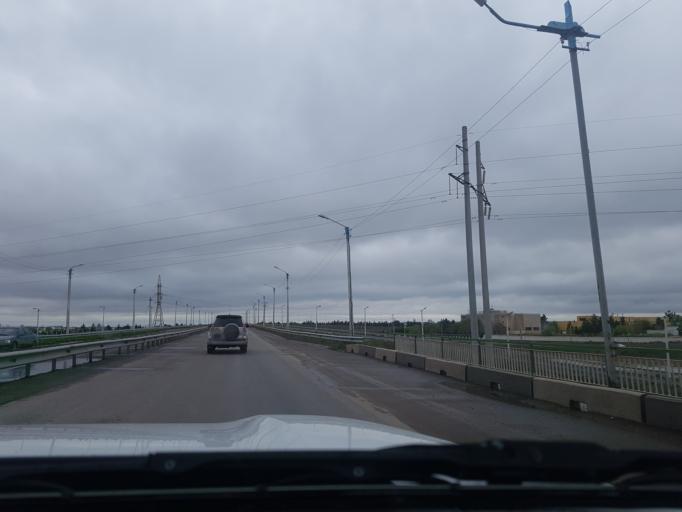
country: TM
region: Mary
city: Mary
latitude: 37.5932
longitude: 61.8853
